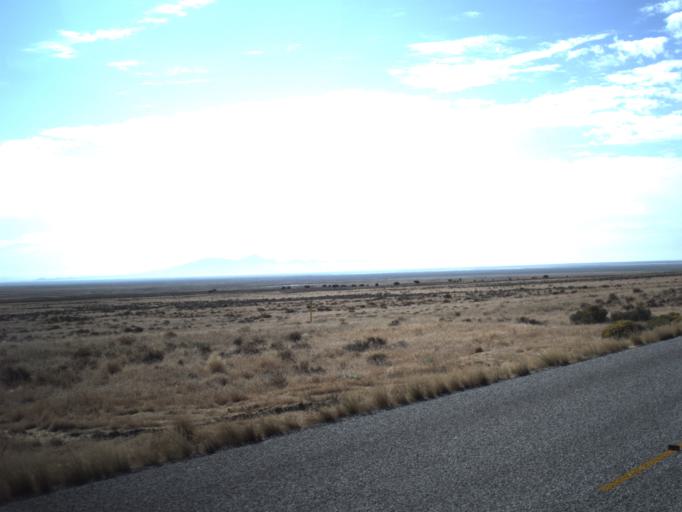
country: US
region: Utah
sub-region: Tooele County
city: Wendover
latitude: 41.5146
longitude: -113.5995
